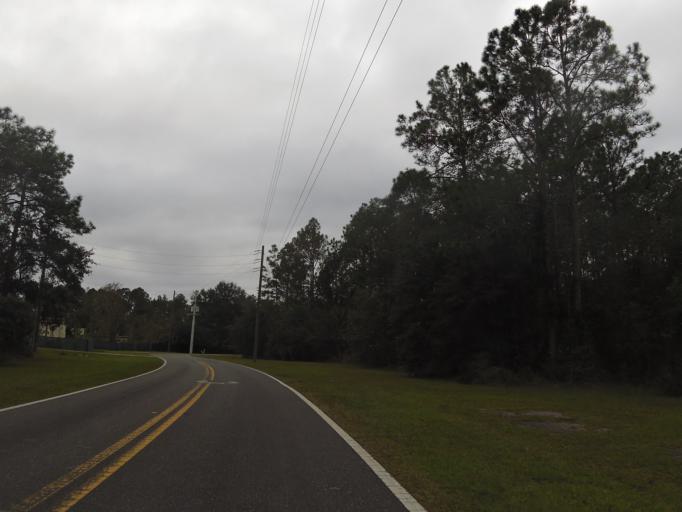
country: US
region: Florida
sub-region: Duval County
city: Baldwin
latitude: 30.2247
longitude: -81.8948
